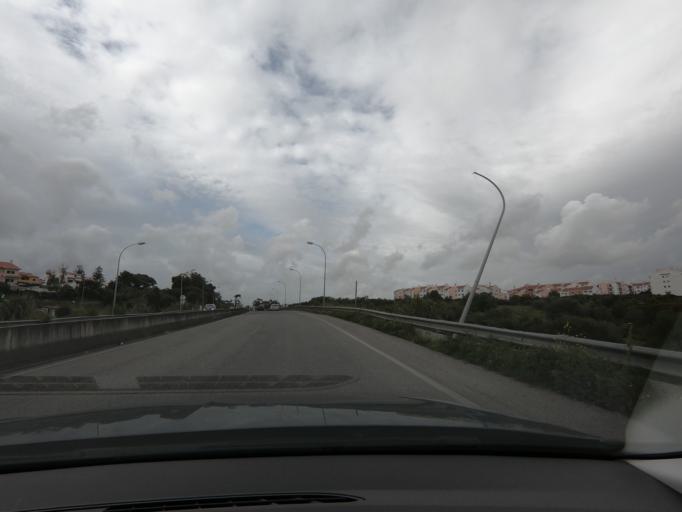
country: PT
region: Lisbon
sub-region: Sintra
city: Rio de Mouro
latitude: 38.7549
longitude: -9.3438
